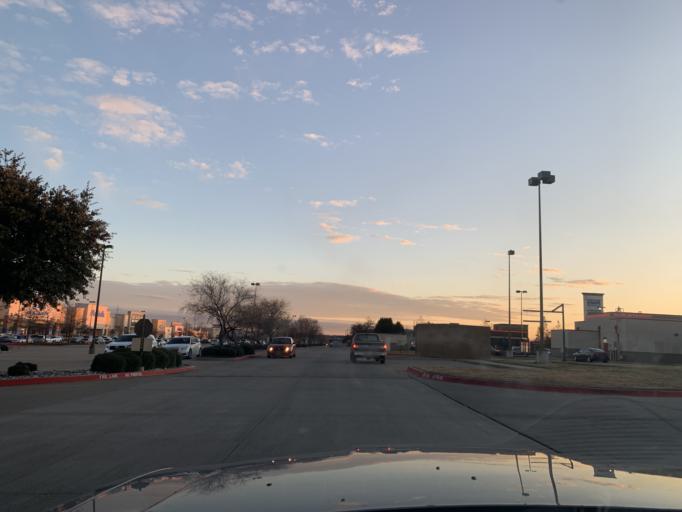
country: US
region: Texas
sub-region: Tarrant County
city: Euless
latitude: 32.8799
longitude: -97.0977
